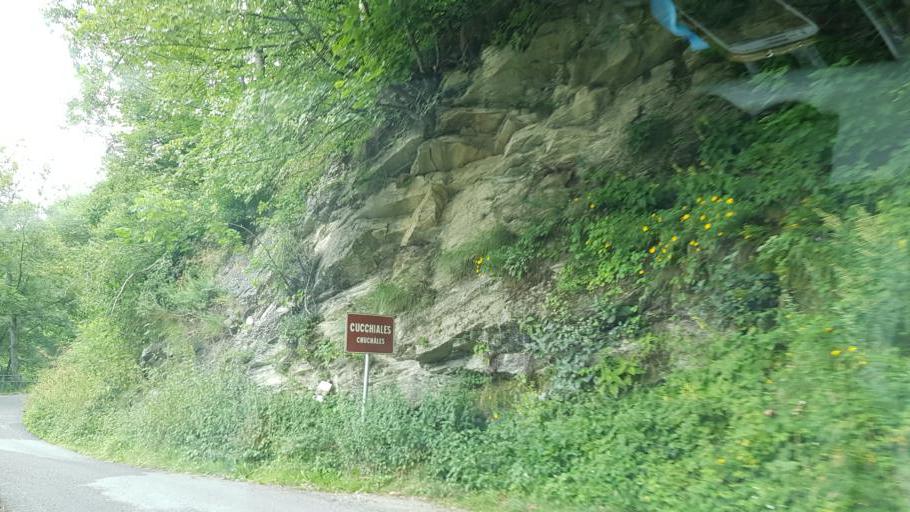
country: IT
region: Piedmont
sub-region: Provincia di Cuneo
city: Stroppo
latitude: 44.5213
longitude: 7.1282
